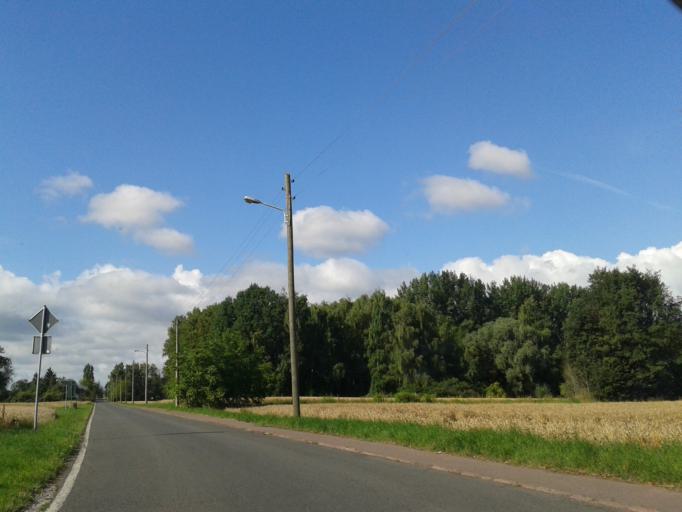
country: DE
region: Saxony-Anhalt
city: Halle (Saale)
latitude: 51.5150
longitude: 12.0045
